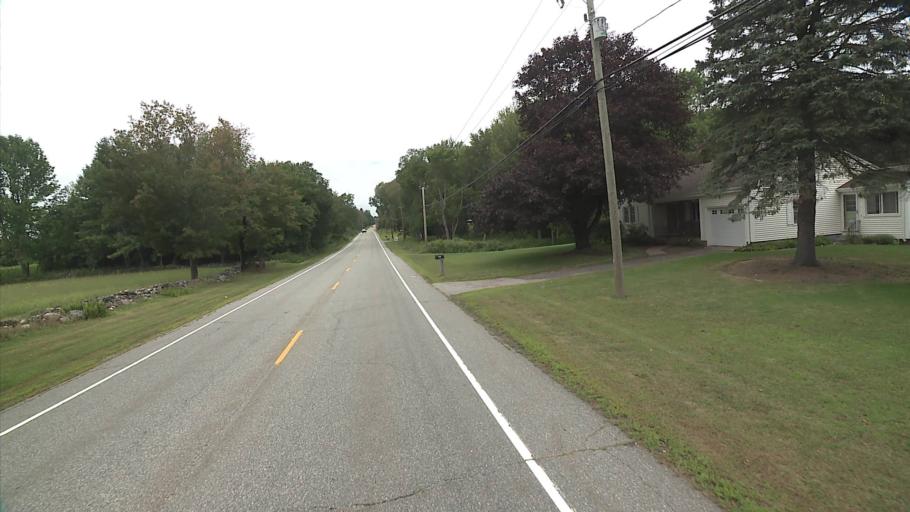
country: US
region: Connecticut
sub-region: Hartford County
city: Manchester
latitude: 41.7510
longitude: -72.4388
